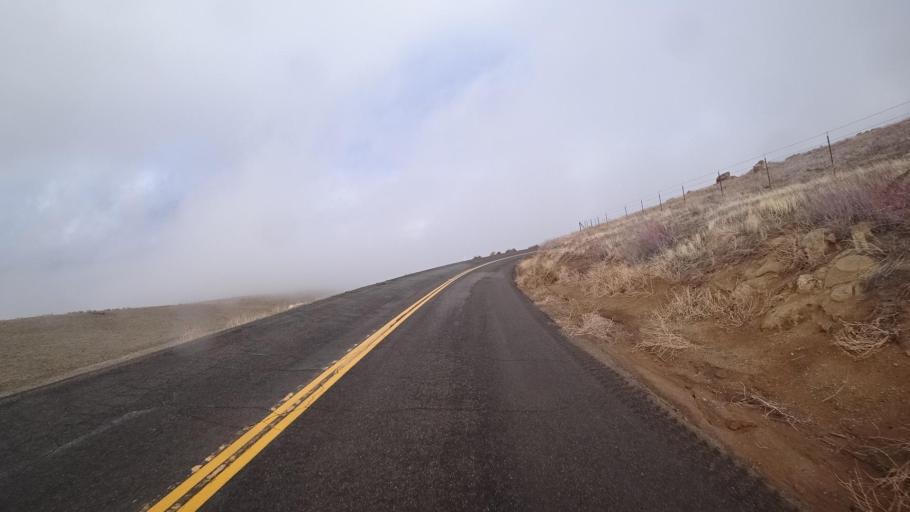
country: US
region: California
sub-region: Kern County
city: Maricopa
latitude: 34.9272
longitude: -119.4125
